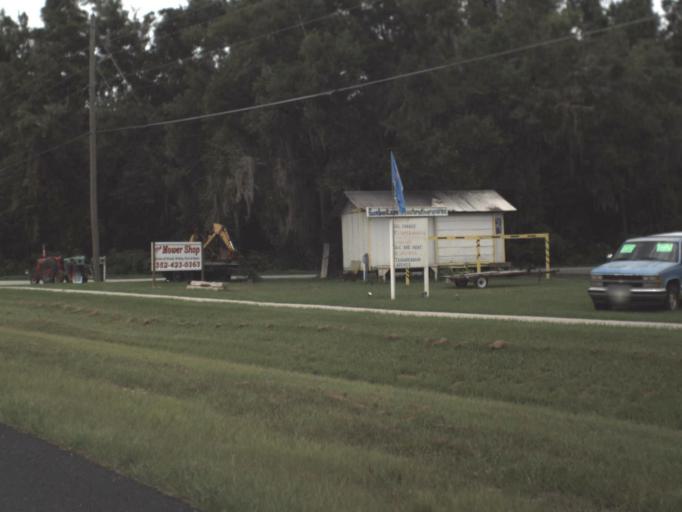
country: US
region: Florida
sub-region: Citrus County
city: Lecanto
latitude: 28.8622
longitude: -82.5066
